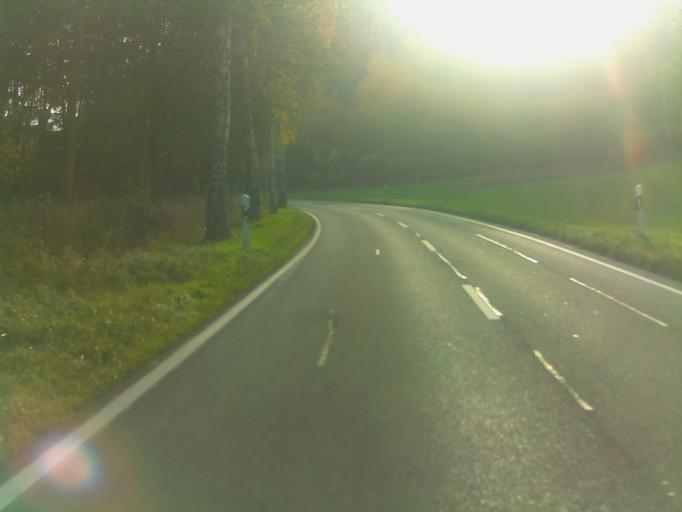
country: DE
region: Rheinland-Pfalz
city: Tiefenthal
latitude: 49.5254
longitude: 8.1040
